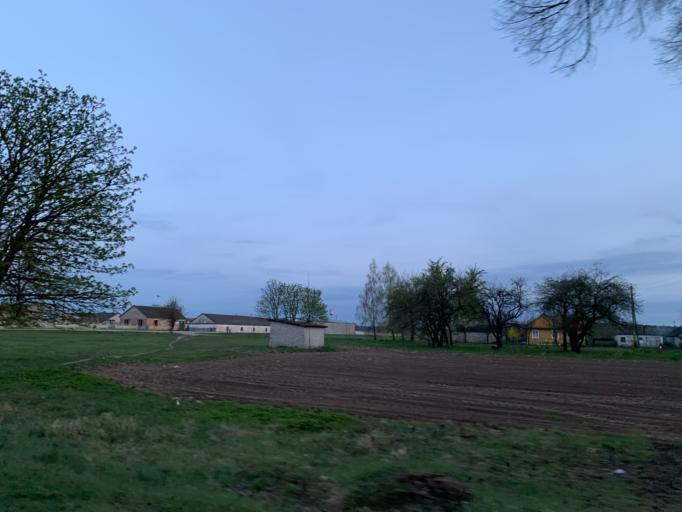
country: BY
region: Minsk
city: Snow
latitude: 53.1668
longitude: 26.5179
